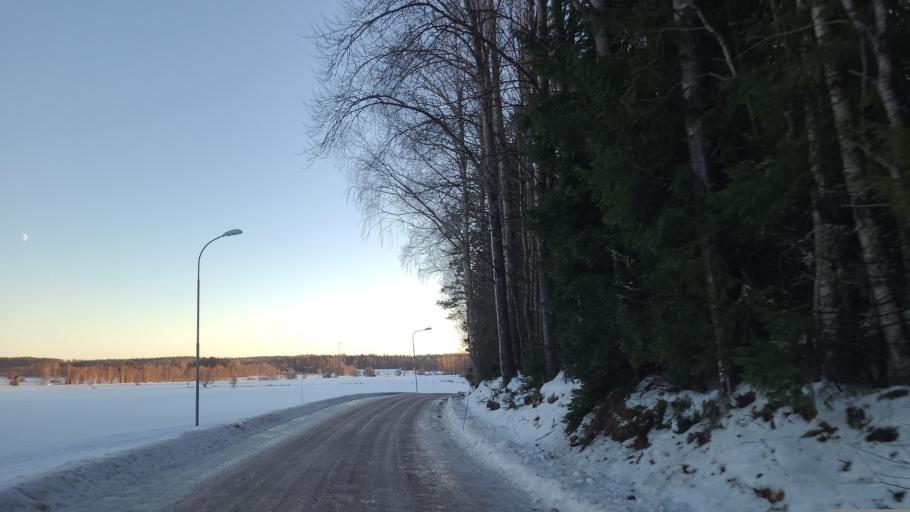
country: SE
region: Gaevleborg
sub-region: Soderhamns Kommun
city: Soderhamn
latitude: 61.2773
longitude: 16.9870
